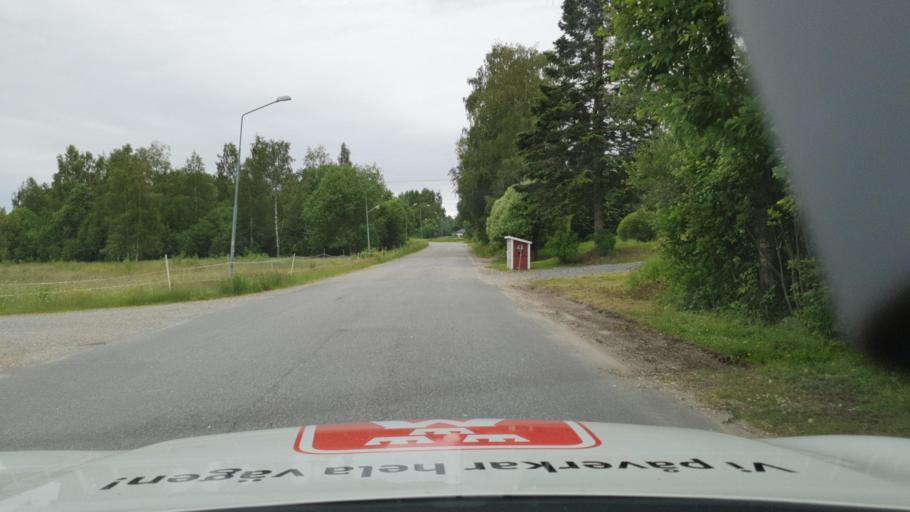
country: SE
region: Vaesterbotten
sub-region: Nordmalings Kommun
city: Nordmaling
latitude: 63.5369
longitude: 19.4434
